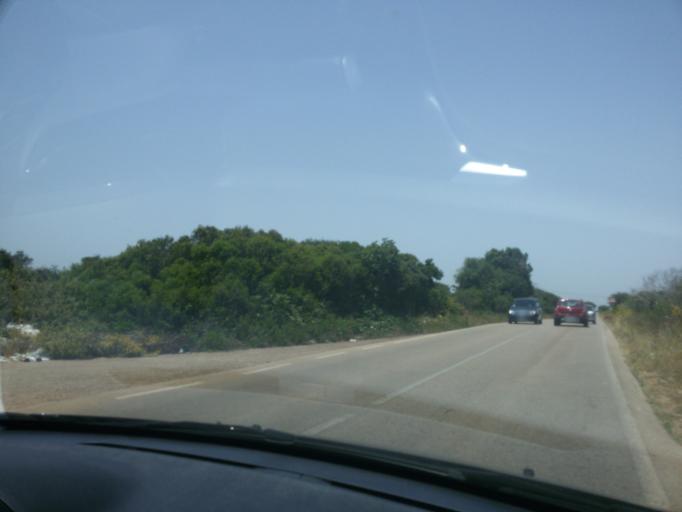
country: IT
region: Apulia
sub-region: Provincia di Brindisi
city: San Pancrazio Salentino
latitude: 40.3377
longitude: 17.8498
